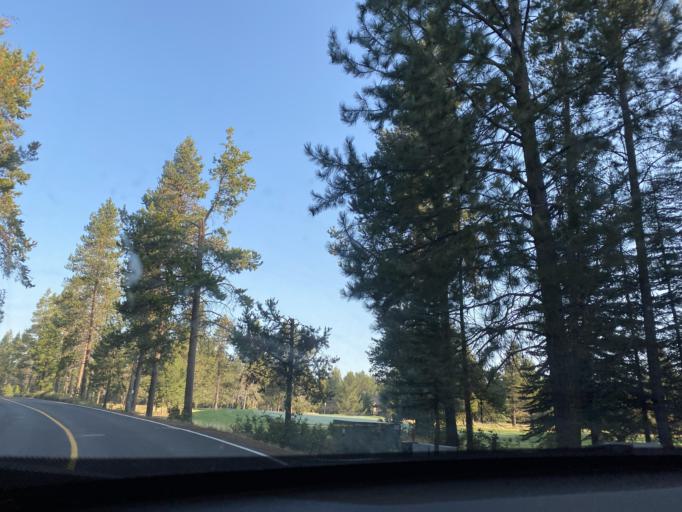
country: US
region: Oregon
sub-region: Deschutes County
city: Sunriver
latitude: 43.8796
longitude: -121.4357
